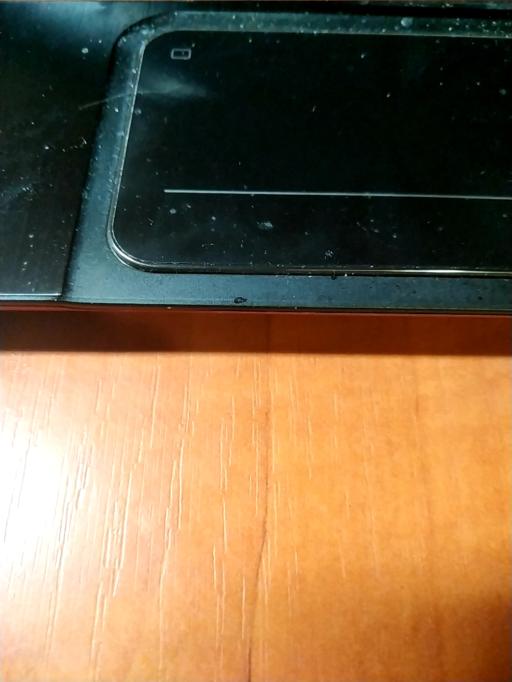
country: RU
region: Tverskaya
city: Ves'yegonsk
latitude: 58.7297
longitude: 37.5438
